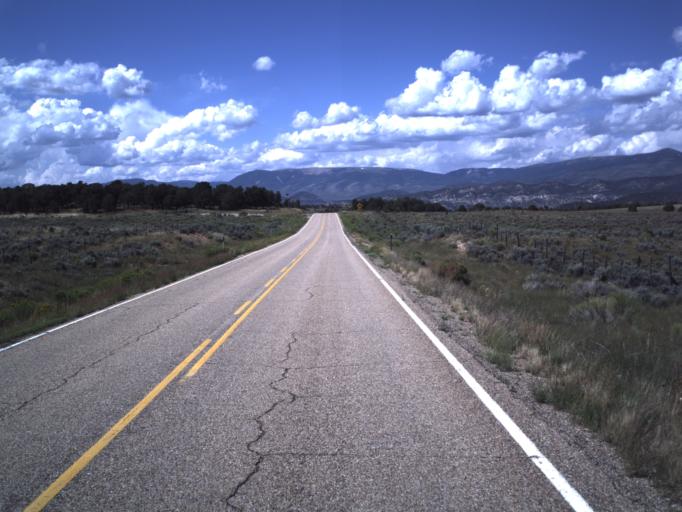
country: US
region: Utah
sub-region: Duchesne County
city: Duchesne
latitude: 40.3043
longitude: -110.6971
